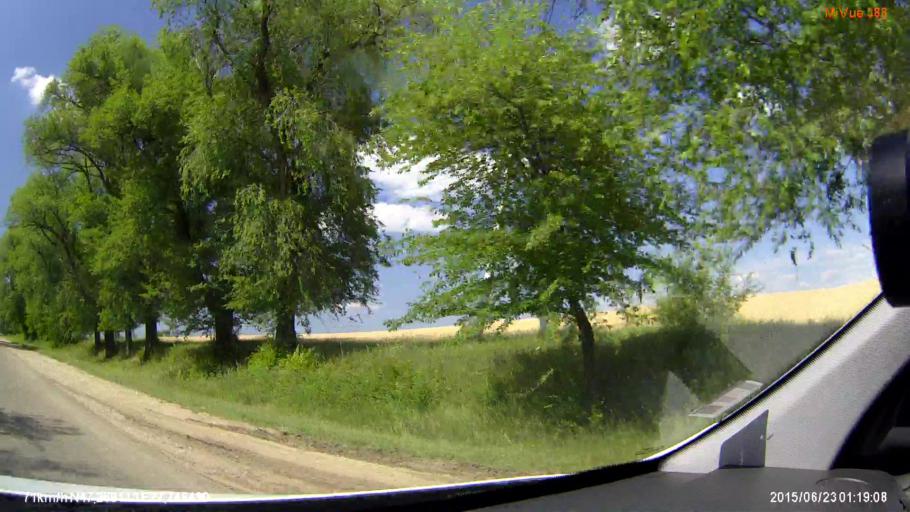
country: RO
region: Iasi
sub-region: Comuna Golaesti
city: Golaesti
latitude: 47.2890
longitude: 27.7466
